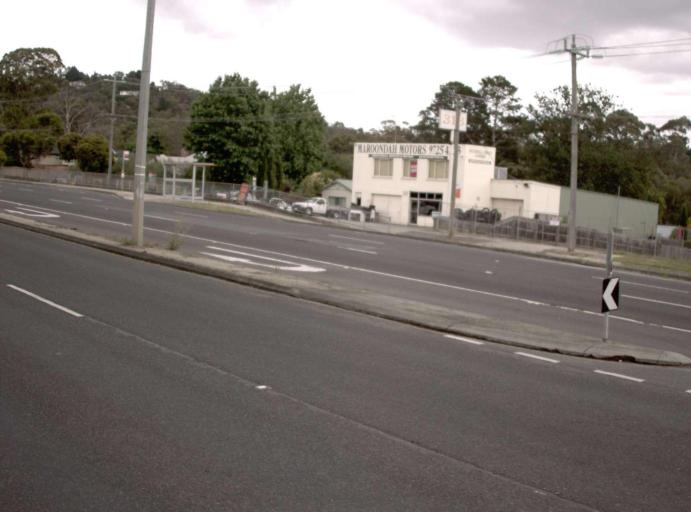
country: AU
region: Victoria
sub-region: Maroondah
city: Croydon North
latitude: -37.7807
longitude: 145.2890
